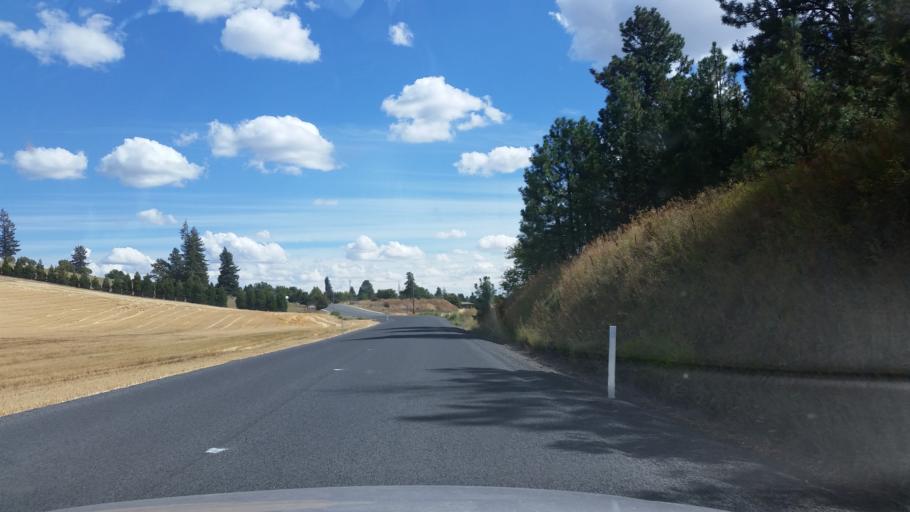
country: US
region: Washington
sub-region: Spokane County
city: Cheney
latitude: 47.4825
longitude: -117.6085
